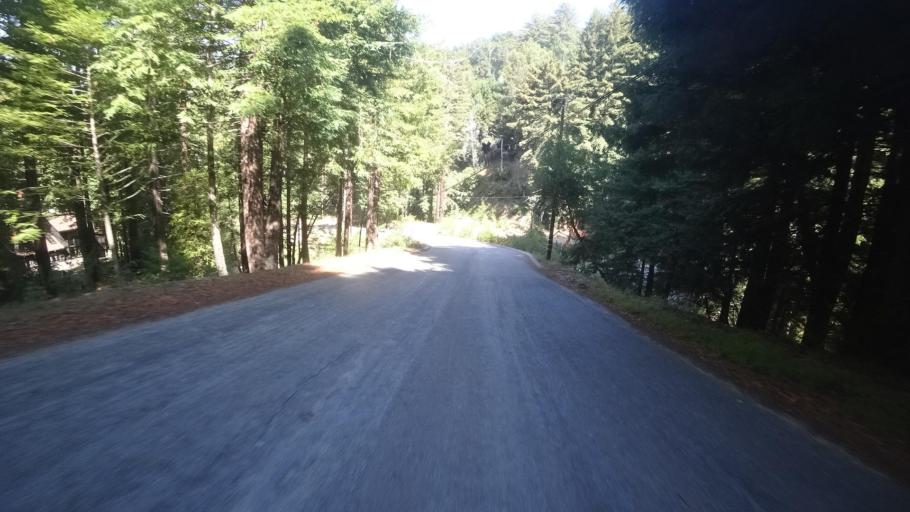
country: US
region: California
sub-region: Monterey County
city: Carmel Valley Village
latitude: 36.3814
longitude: -121.8635
